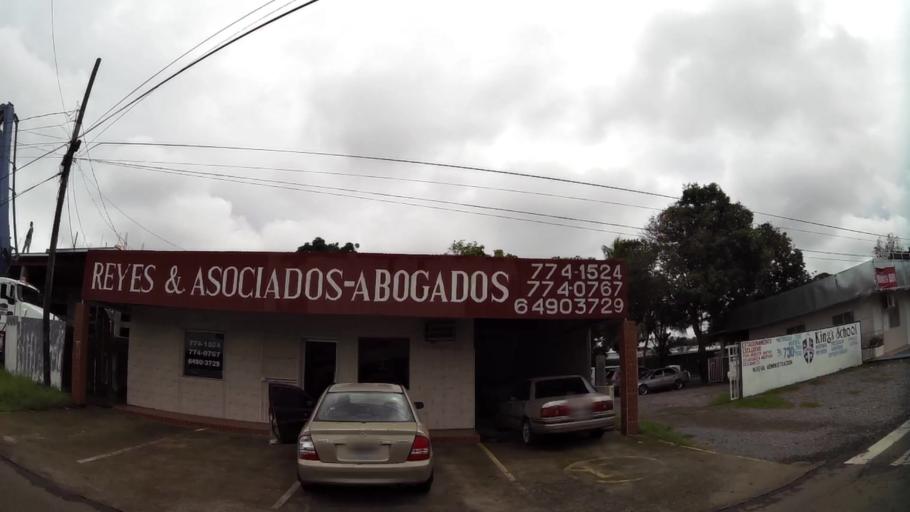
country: PA
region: Chiriqui
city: David
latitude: 8.4222
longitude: -82.4309
